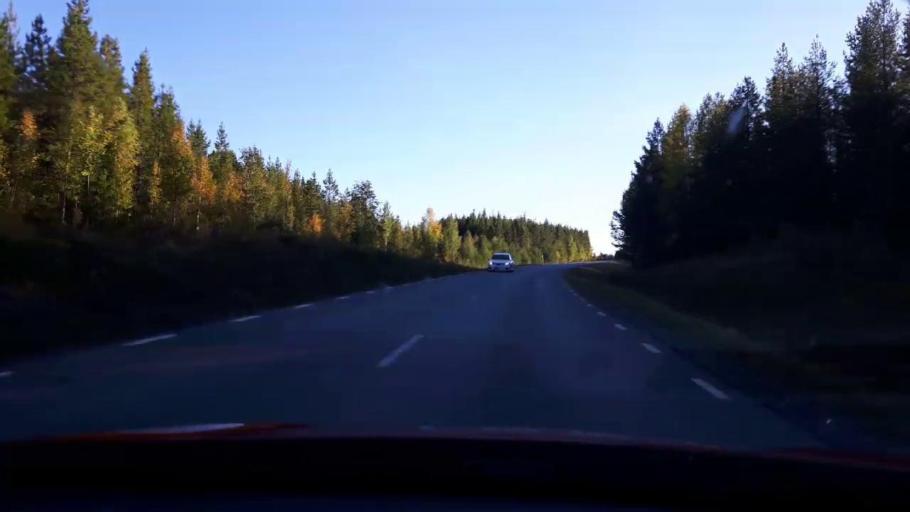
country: SE
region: Jaemtland
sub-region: OEstersunds Kommun
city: Lit
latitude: 63.7617
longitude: 14.7207
